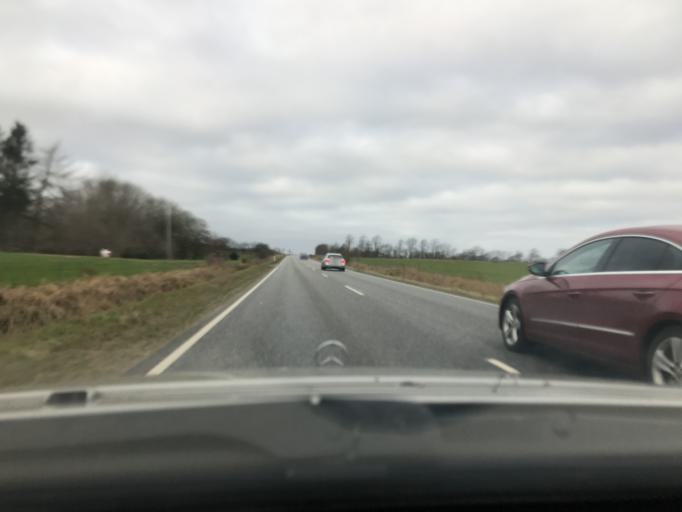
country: DK
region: South Denmark
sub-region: Tonder Kommune
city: Toftlund
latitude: 55.1177
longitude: 9.1605
